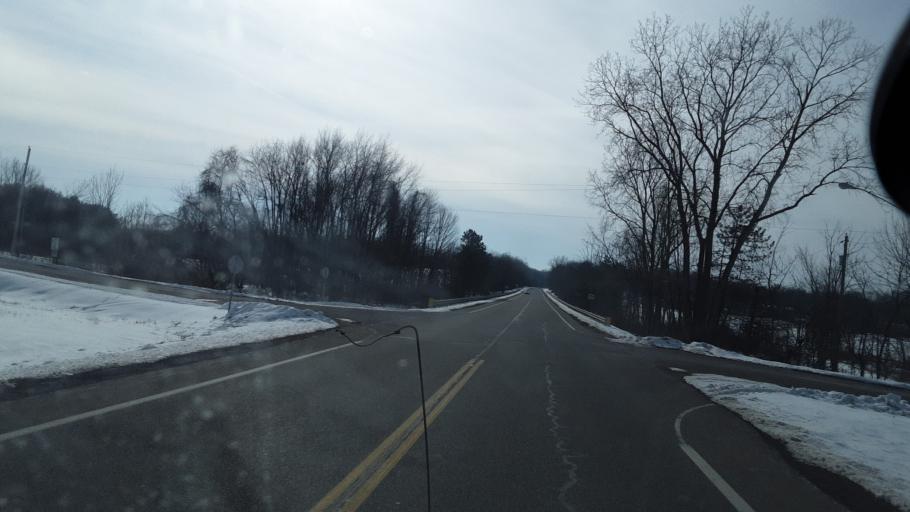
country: US
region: Ohio
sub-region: Stark County
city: Hartville
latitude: 41.0330
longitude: -81.3018
